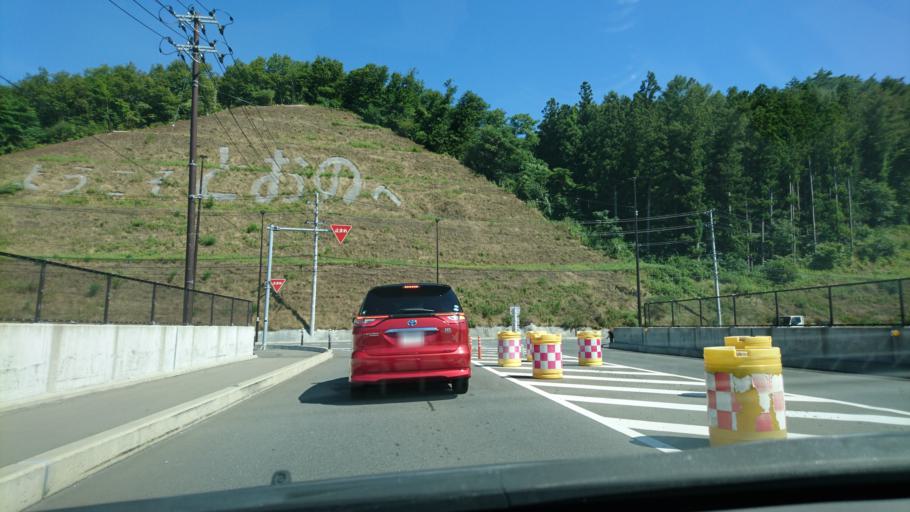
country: JP
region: Iwate
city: Tono
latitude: 39.3319
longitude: 141.5093
